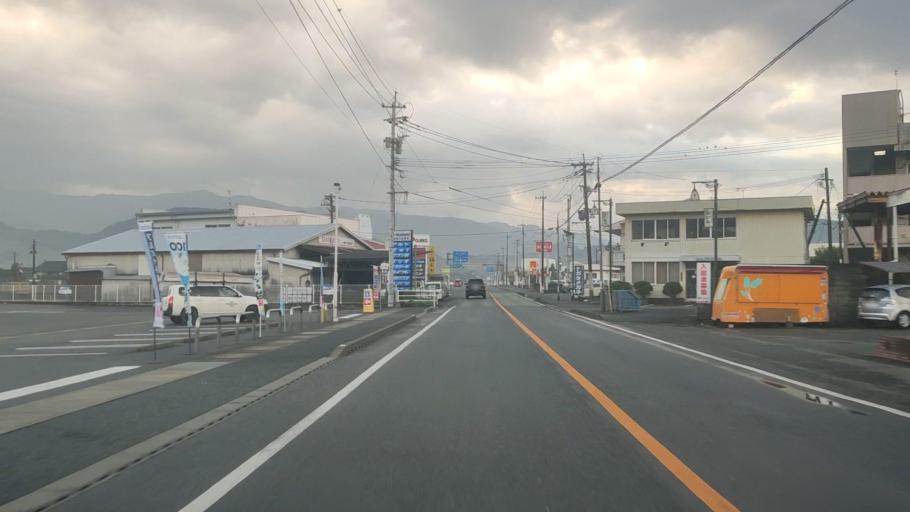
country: JP
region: Kumamoto
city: Matsubase
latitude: 32.6501
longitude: 130.8111
